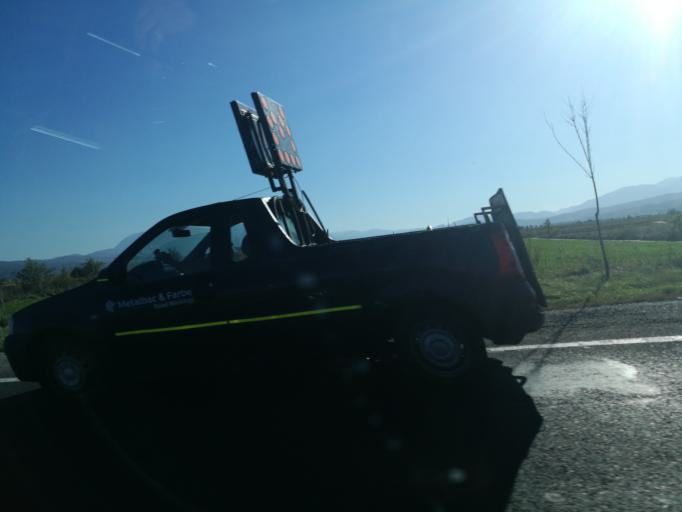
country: RO
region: Brasov
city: Codlea
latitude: 45.6833
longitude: 25.4658
